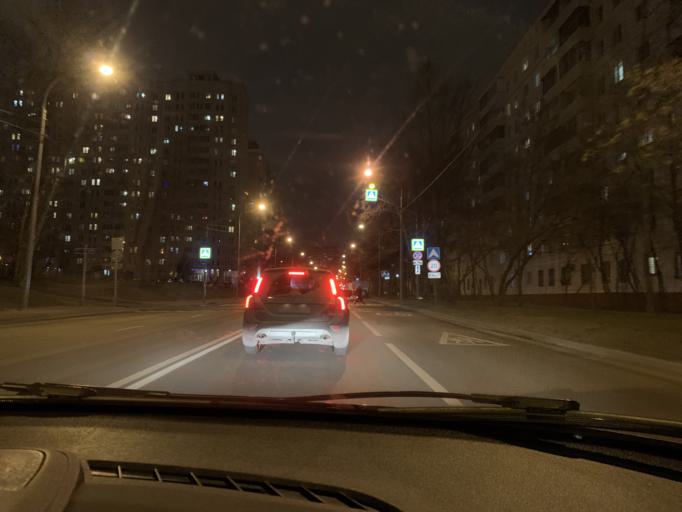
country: RU
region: Moskovskaya
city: Vostochnoe Degunino
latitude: 55.8712
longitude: 37.5605
